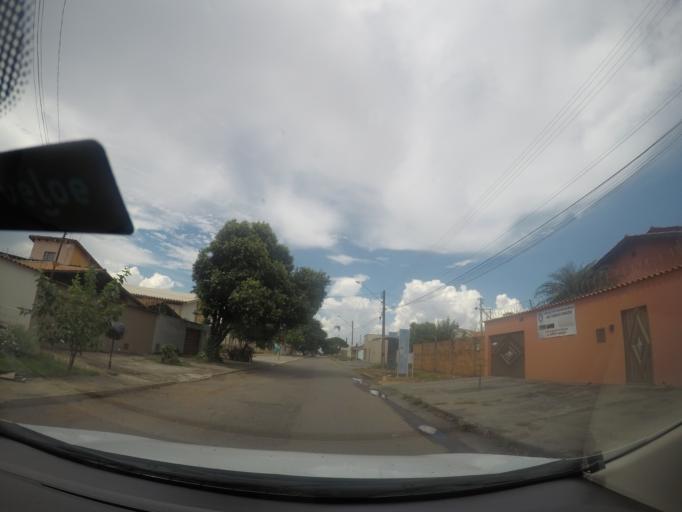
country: BR
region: Goias
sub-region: Goiania
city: Goiania
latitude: -16.7506
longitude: -49.3371
